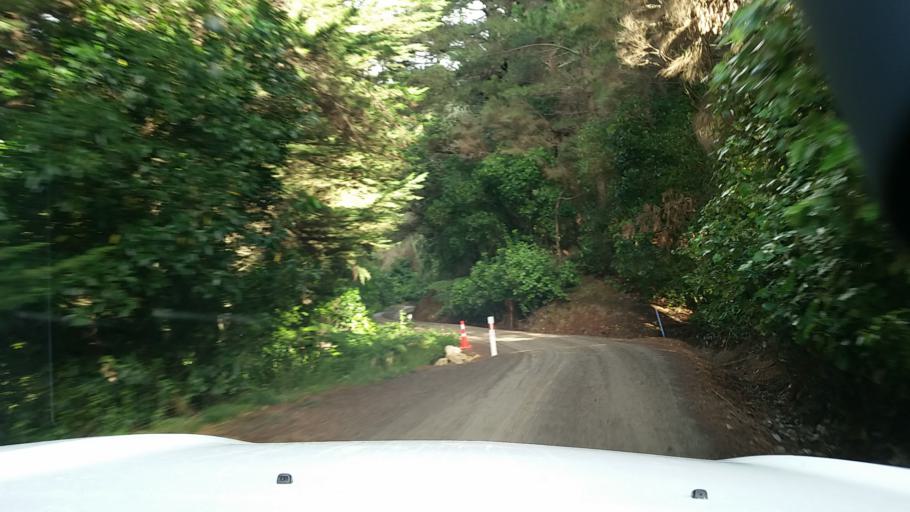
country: NZ
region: Wellington
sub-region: South Wairarapa District
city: Waipawa
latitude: -41.2585
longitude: 175.6193
